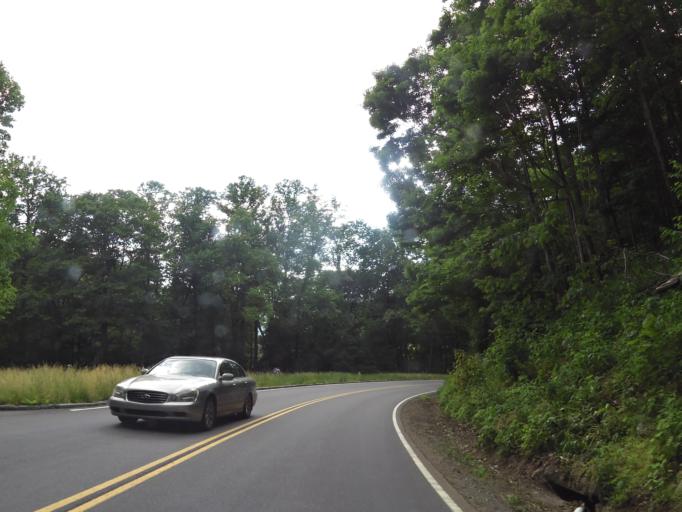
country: US
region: Tennessee
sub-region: Sevier County
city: Gatlinburg
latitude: 35.6395
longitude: -83.4783
